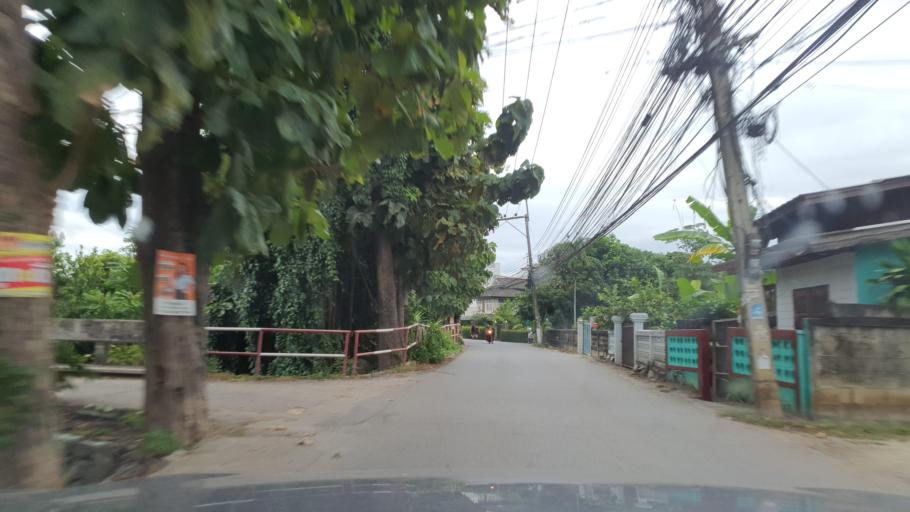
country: TH
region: Chiang Mai
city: San Sai
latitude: 18.9191
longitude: 98.9552
